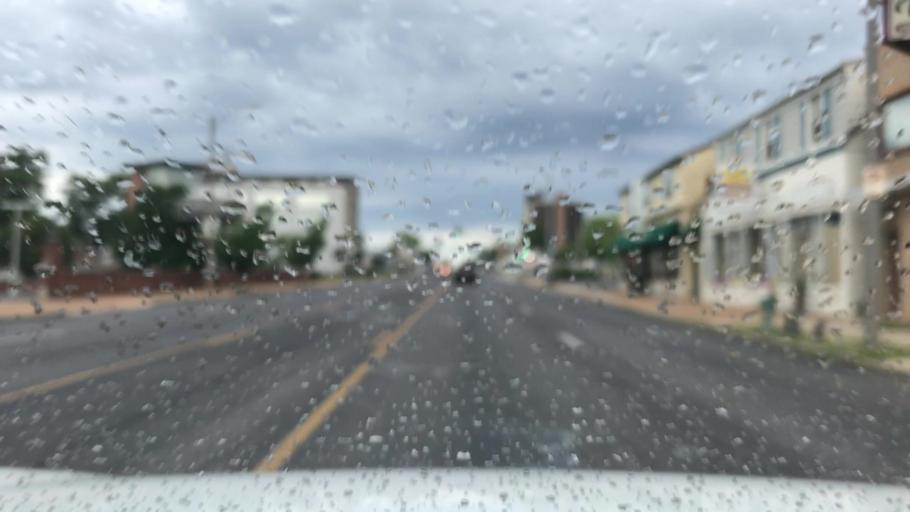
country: US
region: Missouri
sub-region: Saint Louis County
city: Maplewood
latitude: 38.5929
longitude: -90.3009
